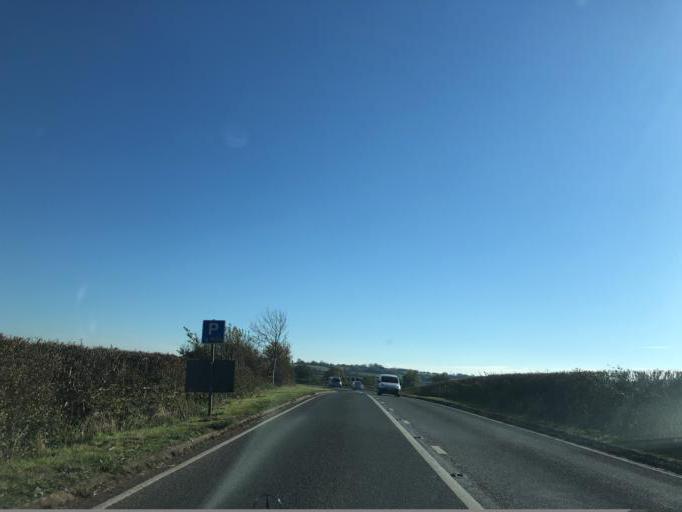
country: GB
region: England
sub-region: Warwickshire
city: Harbury
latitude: 52.2669
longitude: -1.4693
